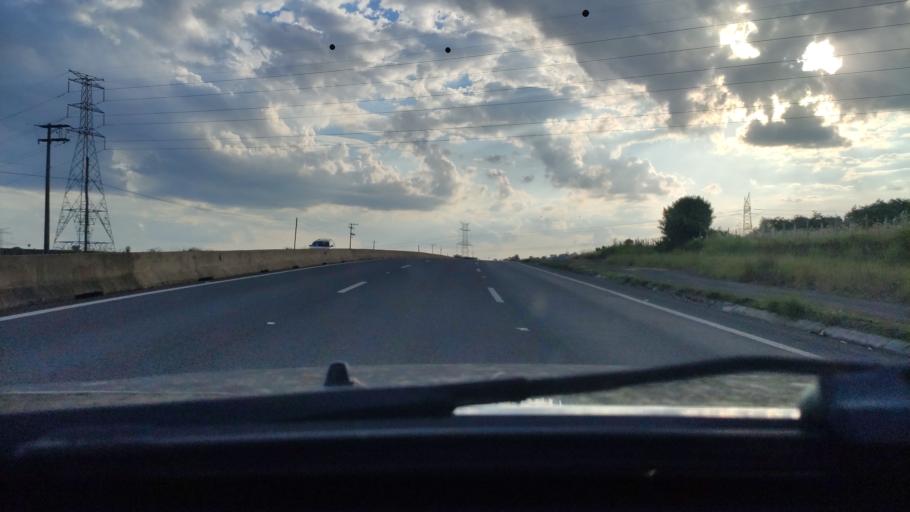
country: BR
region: Sao Paulo
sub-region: Mogi-Mirim
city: Mogi Mirim
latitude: -22.4499
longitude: -47.0619
